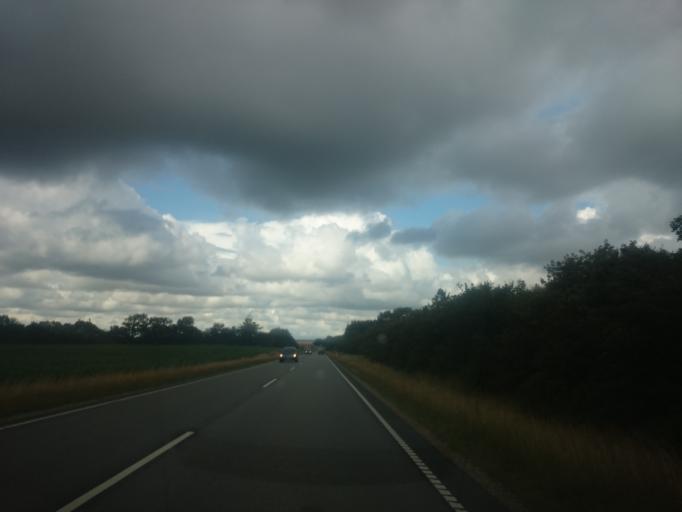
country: DK
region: South Denmark
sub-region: Billund Kommune
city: Grindsted
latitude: 55.6885
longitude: 8.9674
